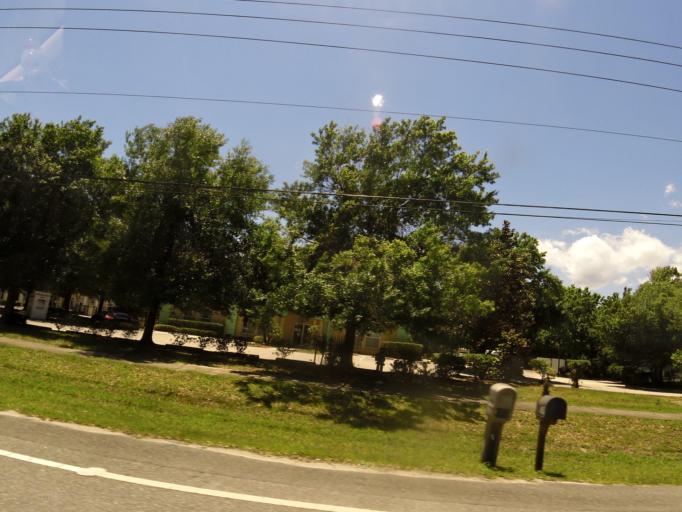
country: US
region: Florida
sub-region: Flagler County
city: Flagler Beach
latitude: 29.4740
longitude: -81.1776
